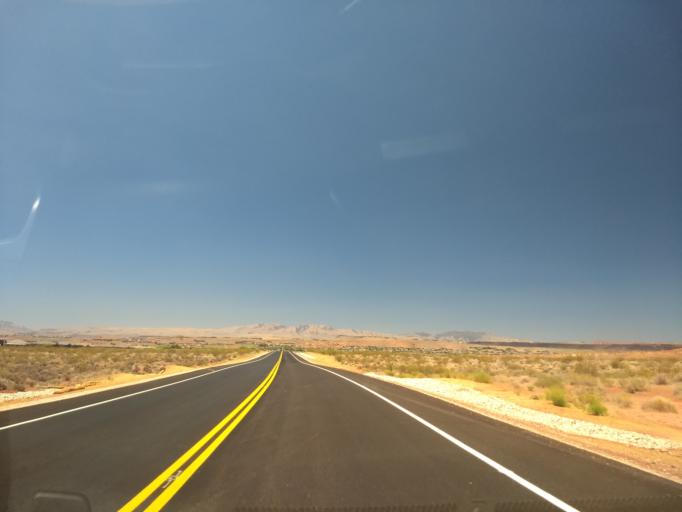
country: US
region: Utah
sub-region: Washington County
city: Washington
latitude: 37.1497
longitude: -113.4976
